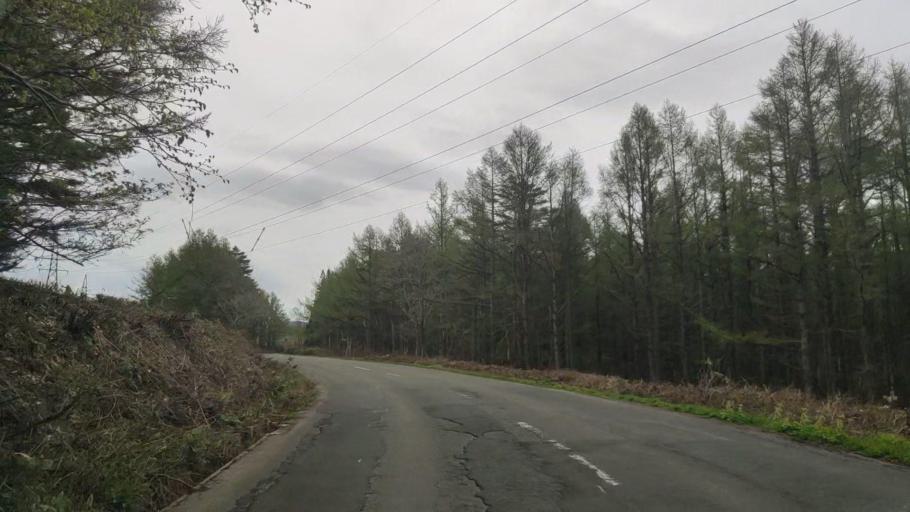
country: JP
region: Aomori
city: Aomori Shi
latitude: 40.7289
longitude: 140.8461
